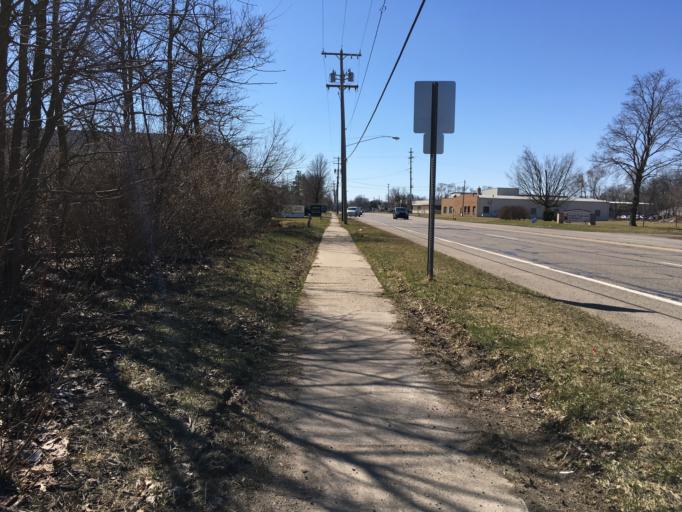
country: US
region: Michigan
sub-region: Kalamazoo County
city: Portage
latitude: 42.1778
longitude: -85.5670
